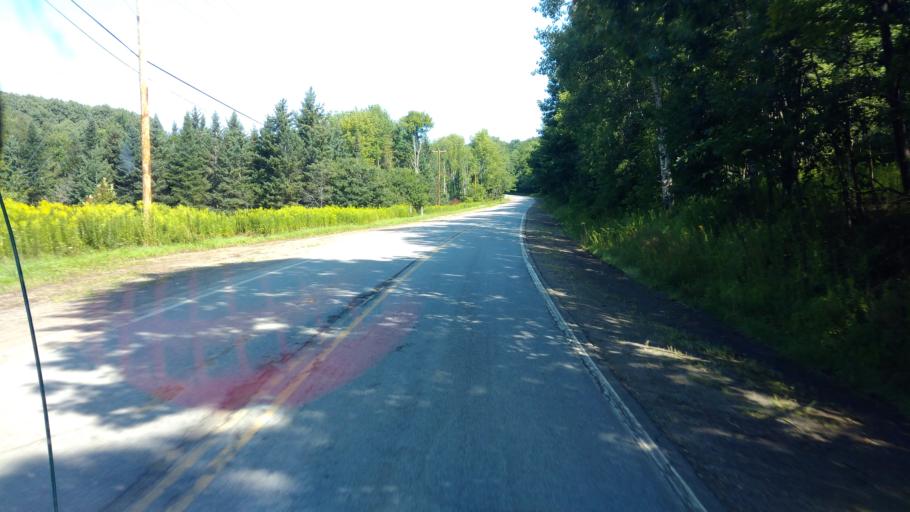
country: US
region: New York
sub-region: Allegany County
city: Bolivar
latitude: 42.1080
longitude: -78.1767
